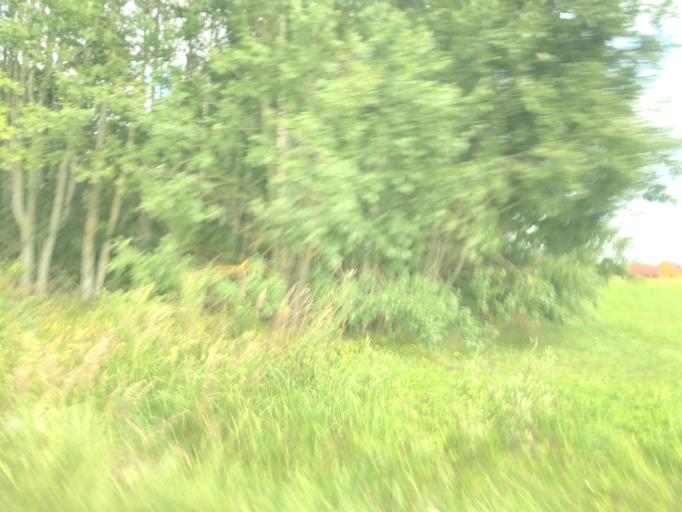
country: LV
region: Vecumnieki
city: Vecumnieki
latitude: 56.4559
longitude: 24.6369
